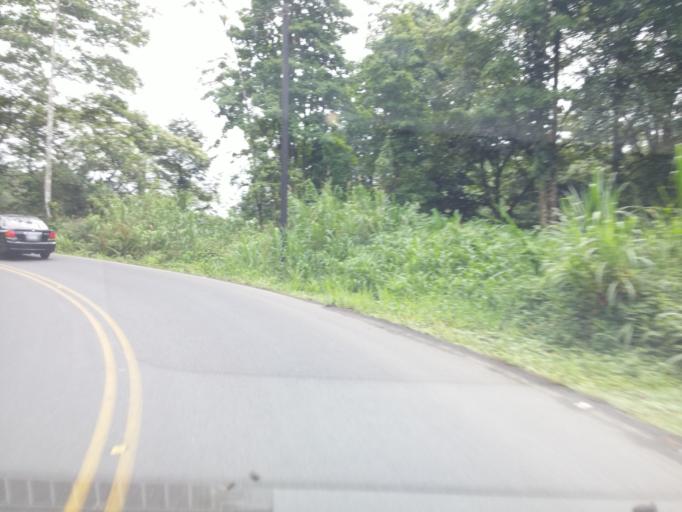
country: CR
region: Alajuela
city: San Ramon
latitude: 10.2174
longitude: -84.5438
